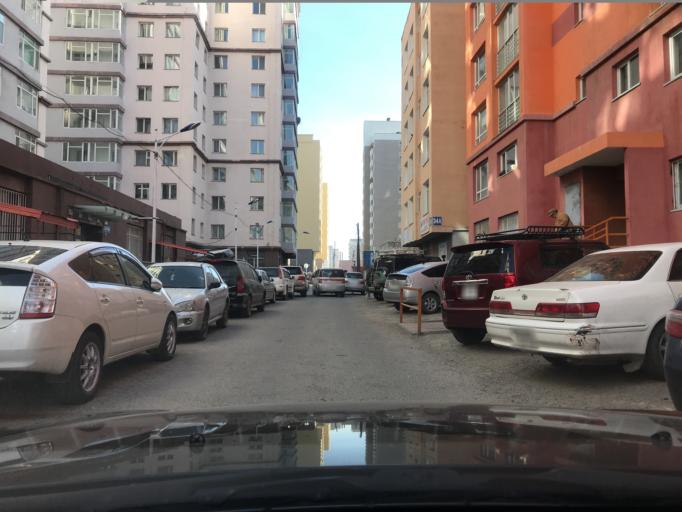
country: MN
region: Ulaanbaatar
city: Ulaanbaatar
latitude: 47.9123
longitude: 106.9453
